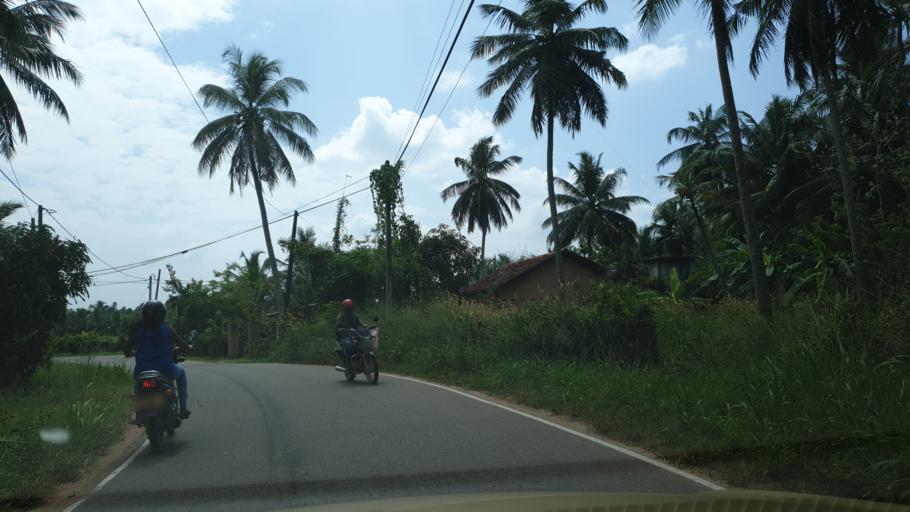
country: LK
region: North Western
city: Kuliyapitiya
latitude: 7.3544
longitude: 79.9674
